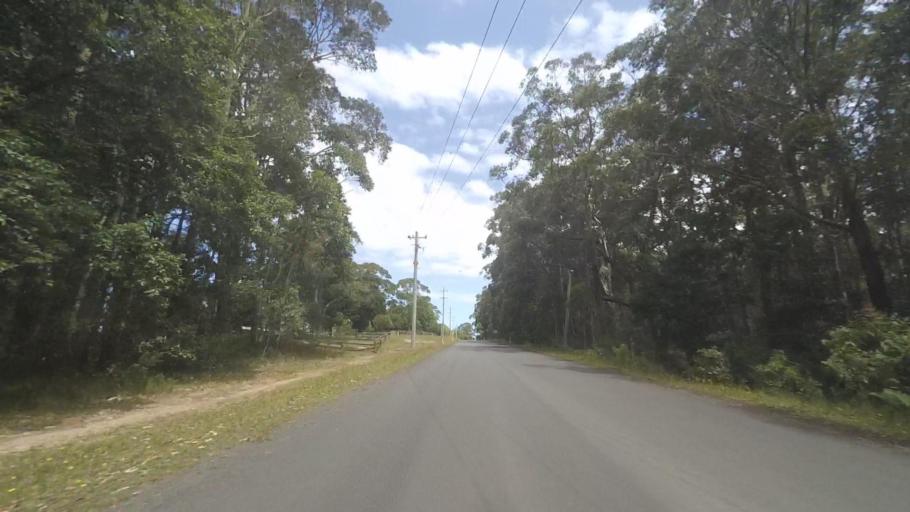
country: AU
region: New South Wales
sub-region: Shoalhaven Shire
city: Milton
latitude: -35.3941
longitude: 150.3690
